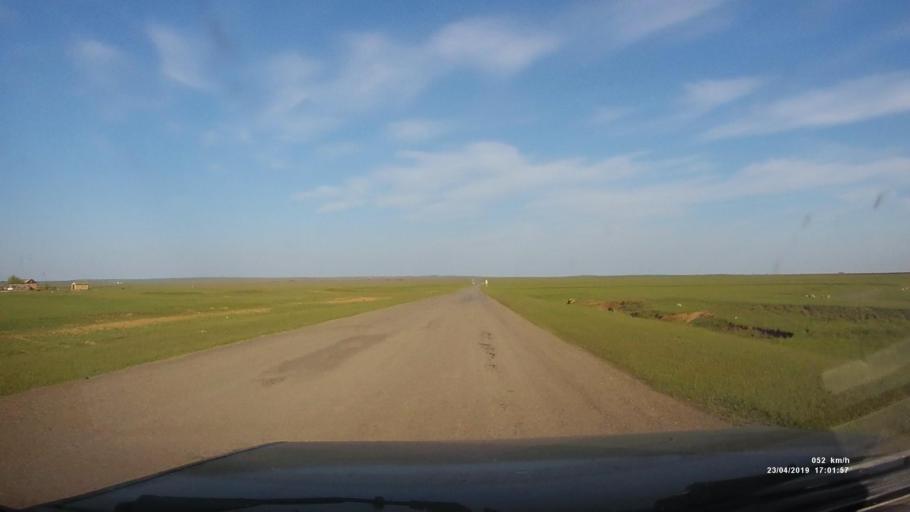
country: RU
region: Kalmykiya
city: Priyutnoye
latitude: 46.2941
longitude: 43.4116
